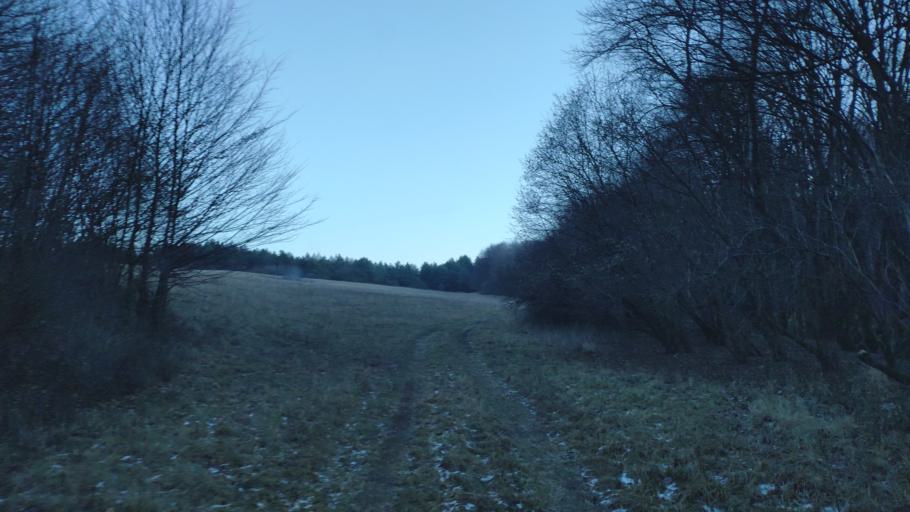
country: SK
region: Kosicky
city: Kosice
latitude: 48.8479
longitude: 21.2422
